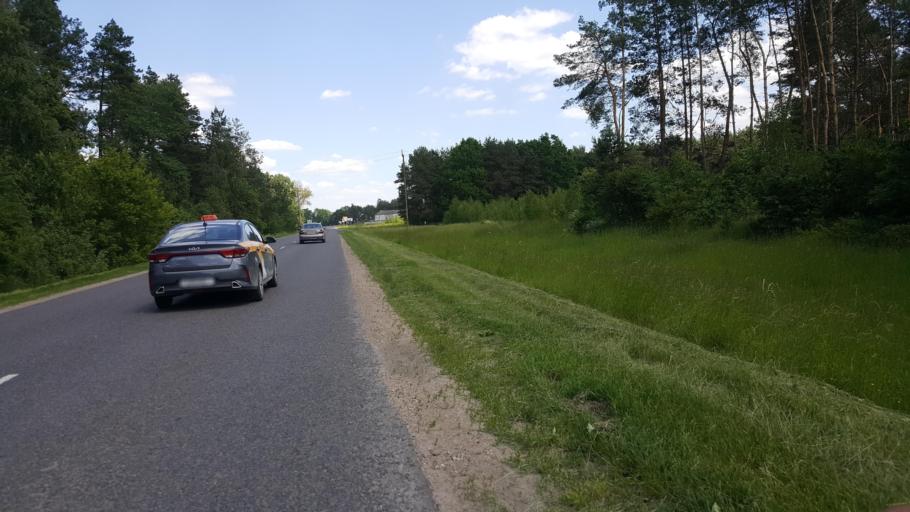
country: BY
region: Brest
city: Kobryn
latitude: 52.2271
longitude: 24.2983
